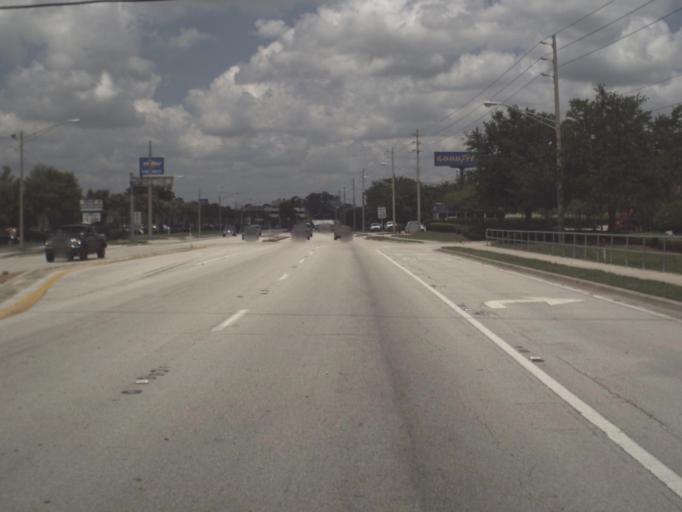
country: US
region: Florida
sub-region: Duval County
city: Jacksonville
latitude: 30.2894
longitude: -81.6348
